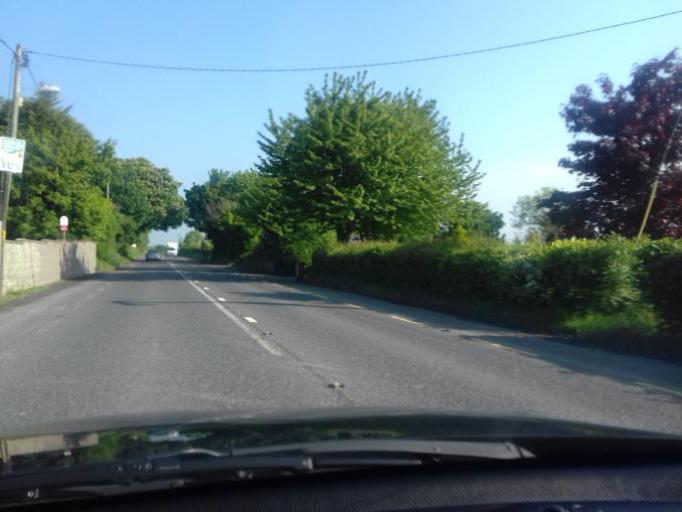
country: IE
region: Leinster
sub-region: Dublin City
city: Finglas
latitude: 53.4286
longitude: -6.3300
